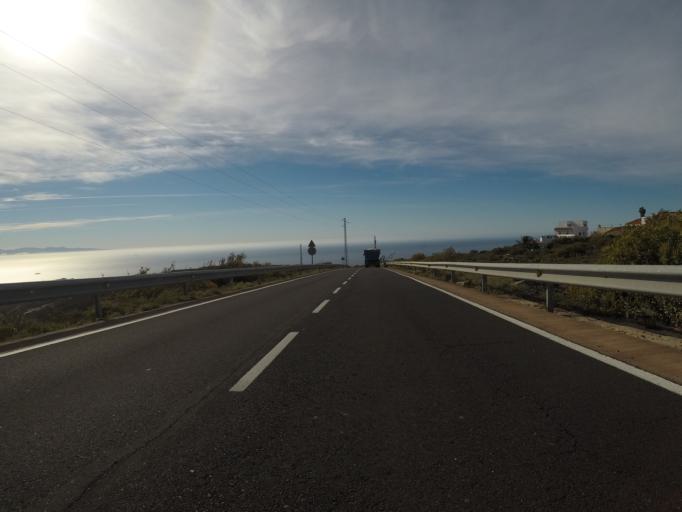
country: ES
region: Canary Islands
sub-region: Provincia de Santa Cruz de Tenerife
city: Lomo de Arico
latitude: 28.1647
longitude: -16.4987
